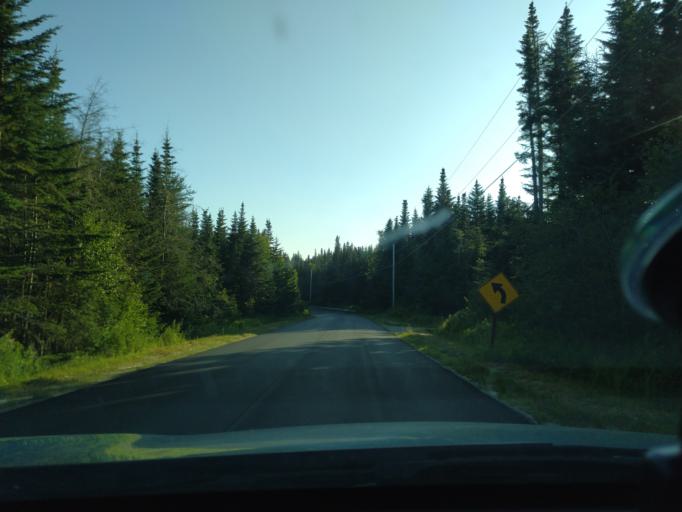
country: US
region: Maine
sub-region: Washington County
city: Machiasport
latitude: 44.6681
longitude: -67.1996
